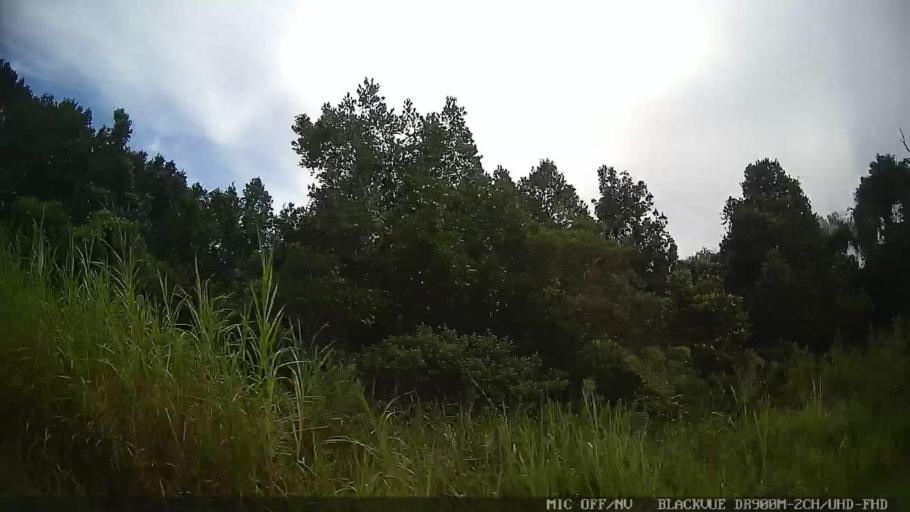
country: BR
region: Sao Paulo
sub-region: Iguape
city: Iguape
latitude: -24.6634
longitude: -47.4257
